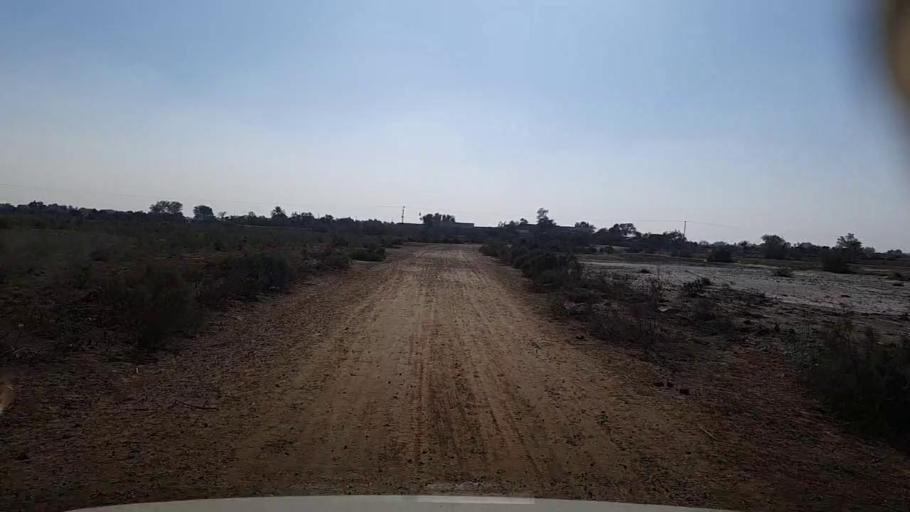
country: PK
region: Sindh
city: Khairpur
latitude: 27.9505
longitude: 69.7515
